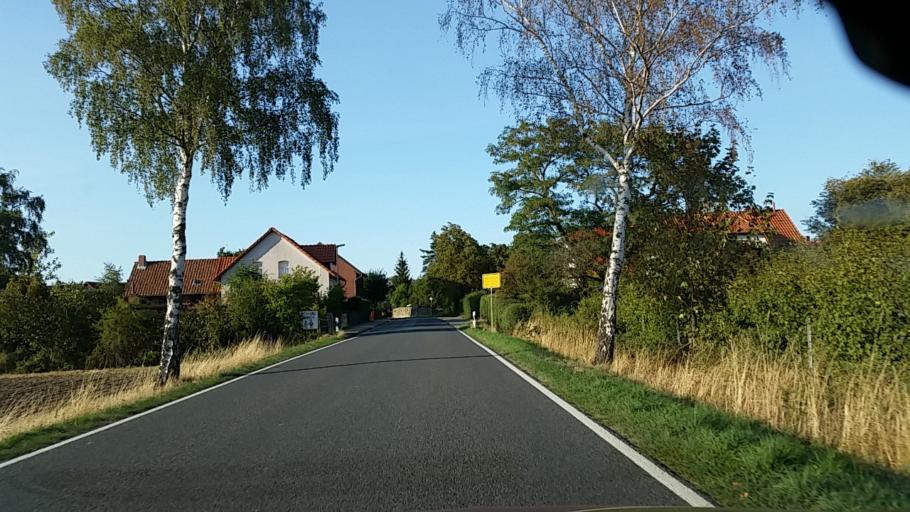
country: DE
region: Lower Saxony
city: Lehre
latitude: 52.3671
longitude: 10.6342
